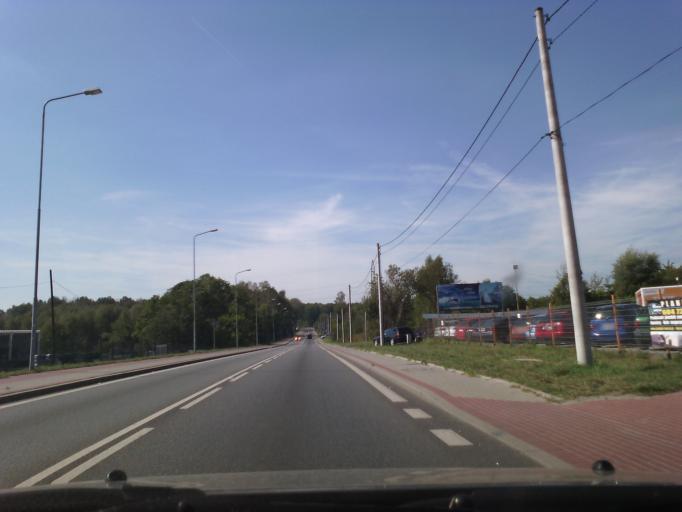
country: PL
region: Silesian Voivodeship
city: Zebrzydowice
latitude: 50.0898
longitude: 18.5088
